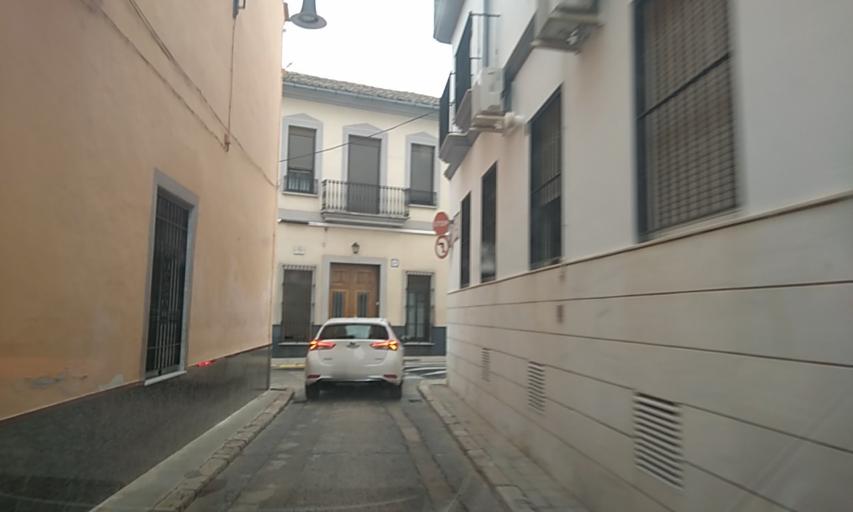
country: ES
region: Valencia
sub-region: Provincia de Valencia
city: L'Alcudia
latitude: 39.1953
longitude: -0.5047
